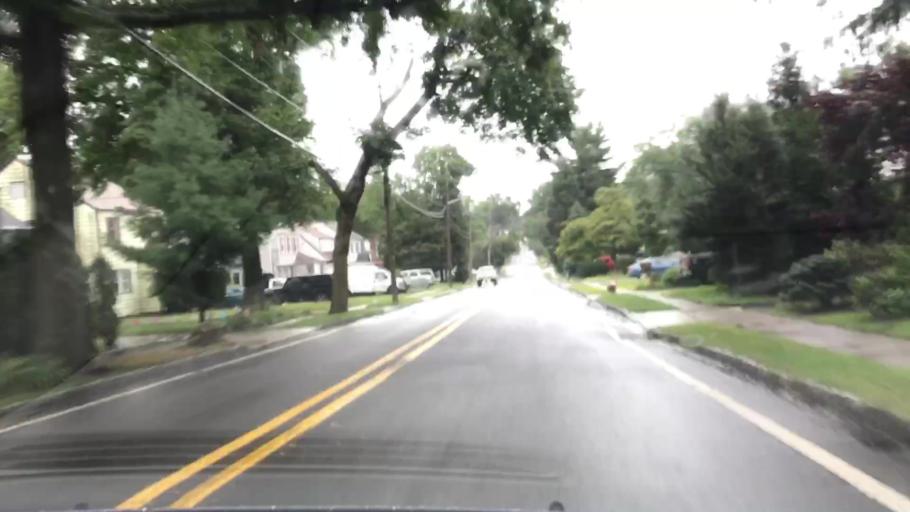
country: US
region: New Jersey
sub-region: Bergen County
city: Englewood
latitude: 40.9033
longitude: -73.9846
